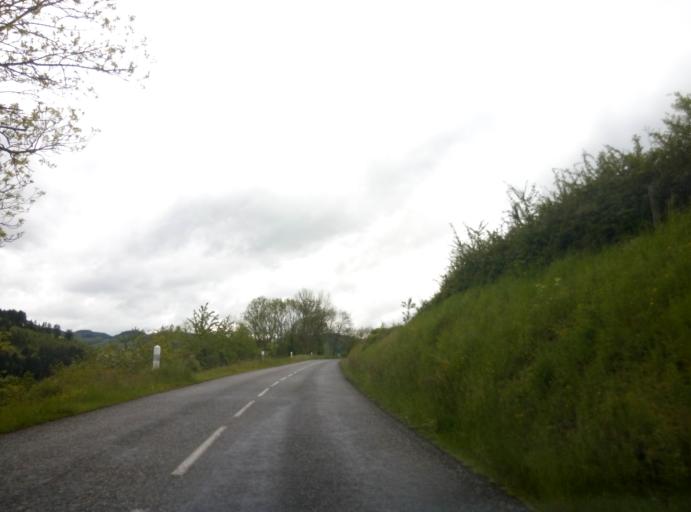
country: FR
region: Rhone-Alpes
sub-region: Departement du Rhone
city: Tarare
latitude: 45.9128
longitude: 4.4288
